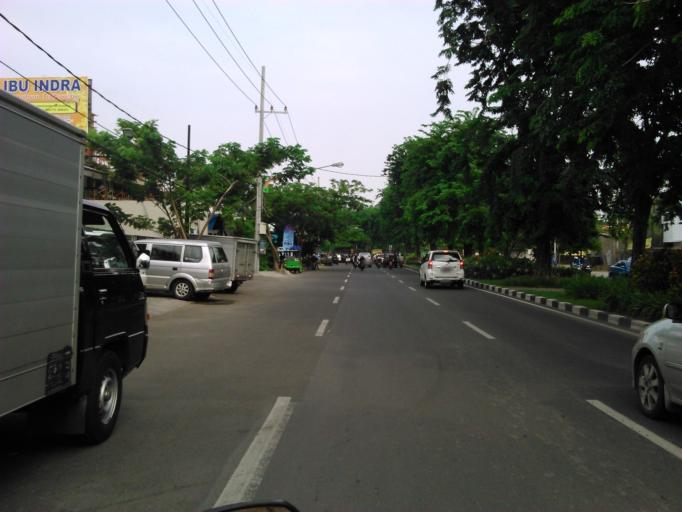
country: ID
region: East Java
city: Brongkalan
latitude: -7.2677
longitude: 112.7709
